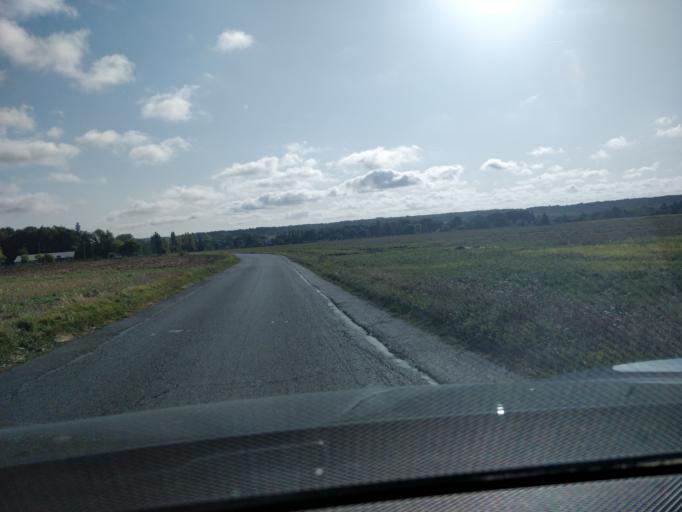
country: FR
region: Ile-de-France
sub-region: Departement de l'Essonne
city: Vaugrigneuse
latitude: 48.6016
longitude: 2.1104
